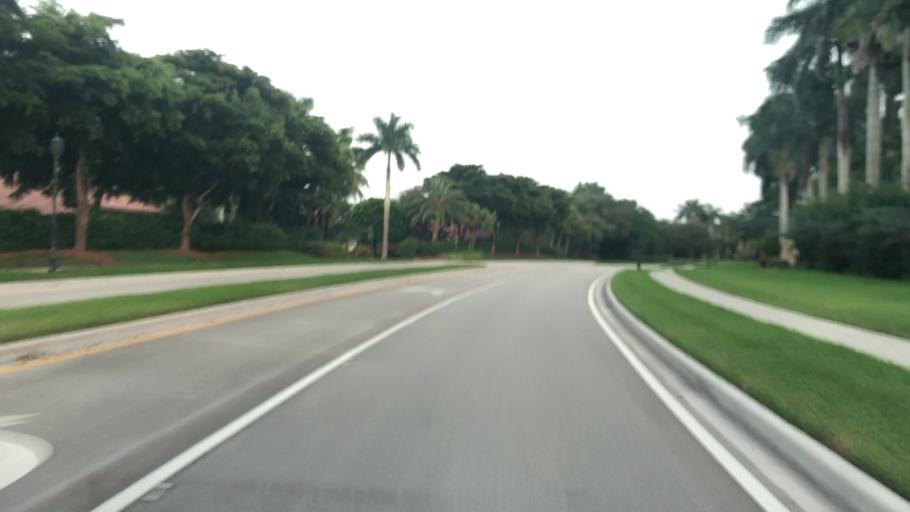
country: US
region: Florida
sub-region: Broward County
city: Weston
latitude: 26.0940
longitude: -80.4017
